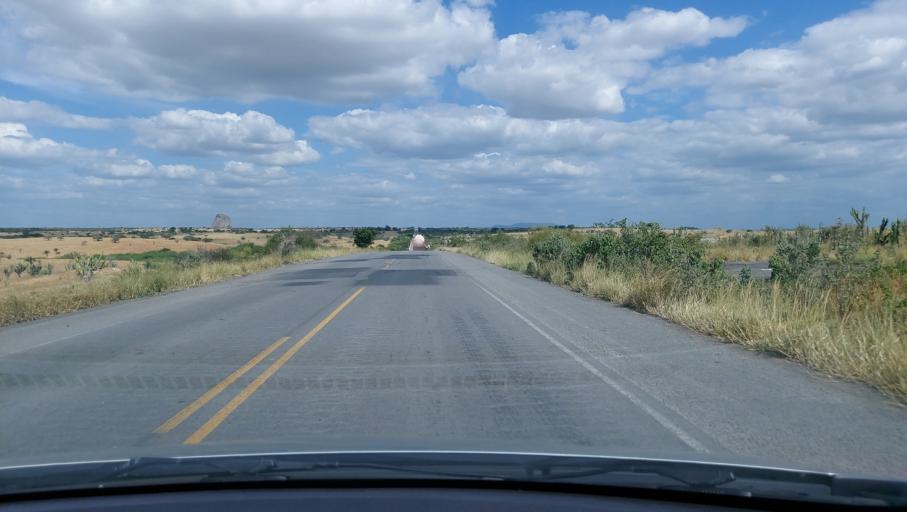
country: BR
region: Bahia
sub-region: Itaberaba
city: Itaberaba
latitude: -12.5208
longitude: -40.1328
